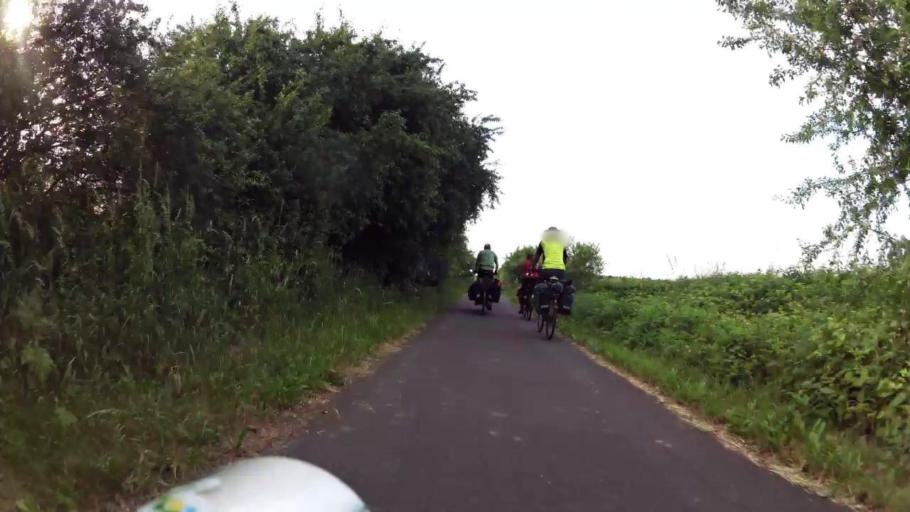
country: PL
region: Kujawsko-Pomorskie
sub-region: Powiat torunski
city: Lubianka
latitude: 53.1379
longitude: 18.4603
